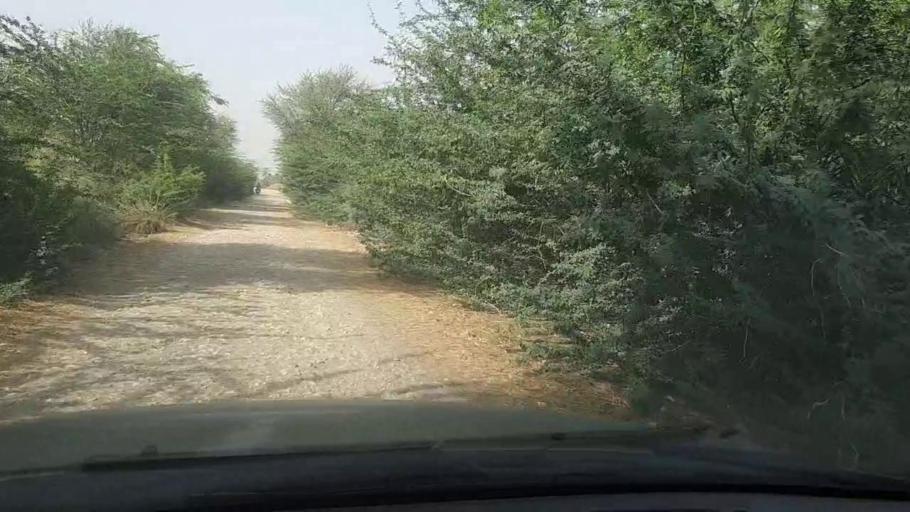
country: PK
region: Sindh
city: Shikarpur
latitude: 27.9028
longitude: 68.5937
